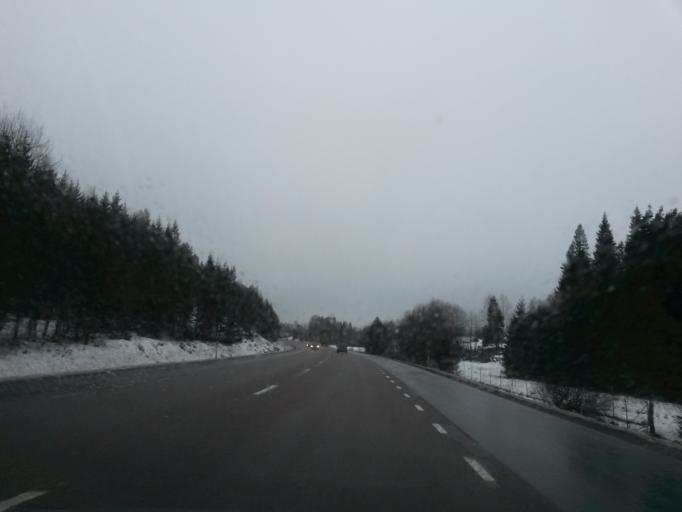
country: SE
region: Vaestra Goetaland
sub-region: Boras Kommun
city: Viskafors
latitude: 57.6438
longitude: 12.9102
